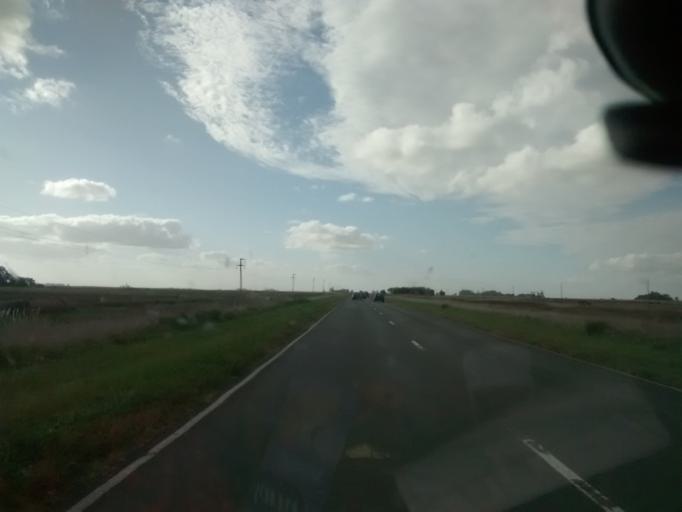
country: AR
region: Buenos Aires
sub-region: Partido de Ayacucho
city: Ayacucho
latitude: -36.8718
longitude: -58.5432
